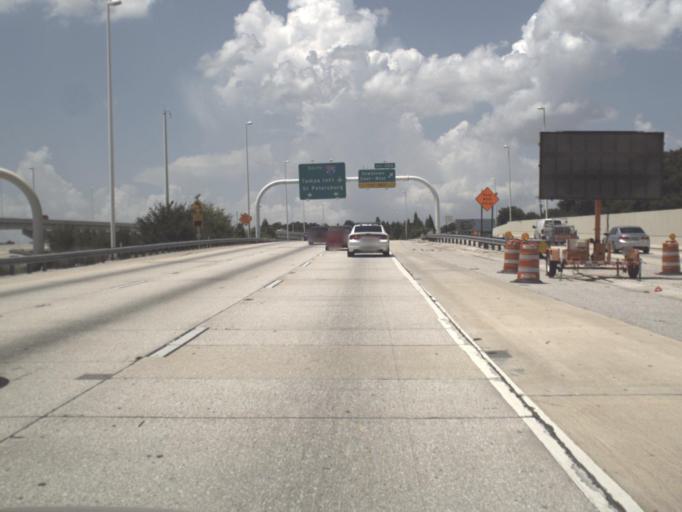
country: US
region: Florida
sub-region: Hillsborough County
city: Tampa
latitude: 27.9651
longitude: -82.4490
